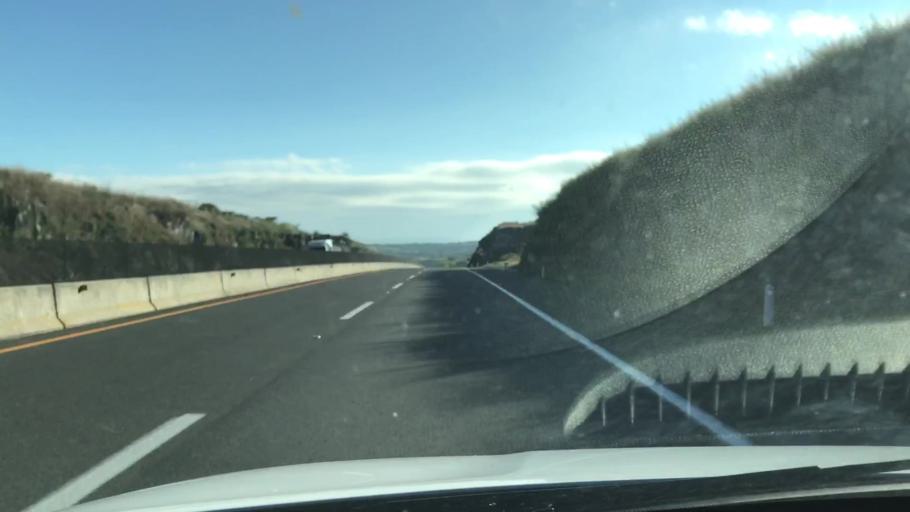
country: MX
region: Jalisco
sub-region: San Juan de los Lagos
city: Colonia Santa Cecilia (La Sauceda)
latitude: 21.1832
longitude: -102.3652
